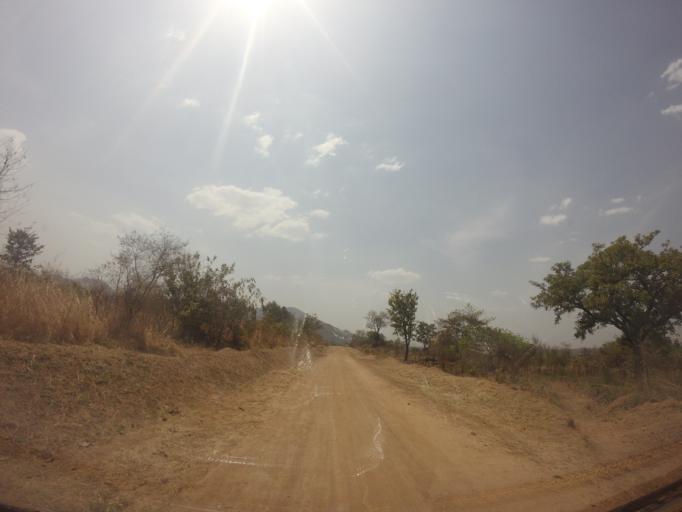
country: UG
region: Northern Region
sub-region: Arua District
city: Arua
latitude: 2.8969
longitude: 31.1222
